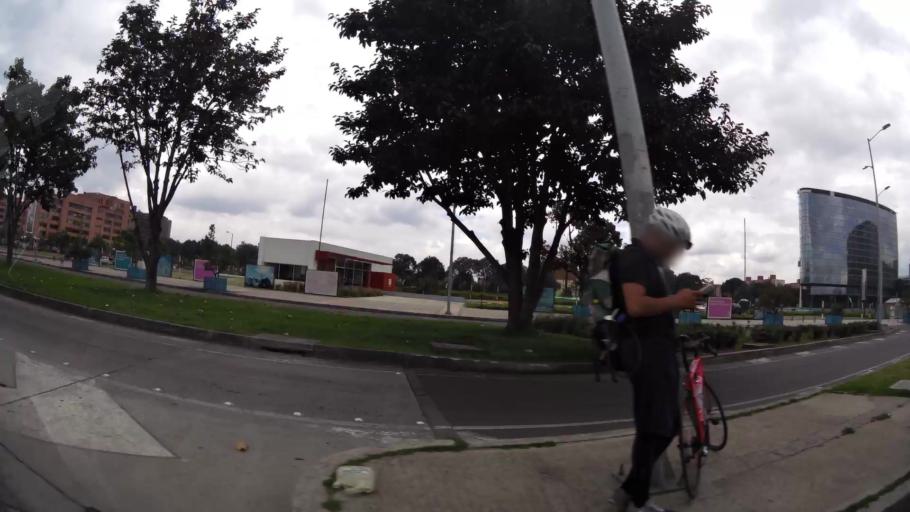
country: CO
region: Bogota D.C.
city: Bogota
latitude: 4.6430
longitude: -74.0971
